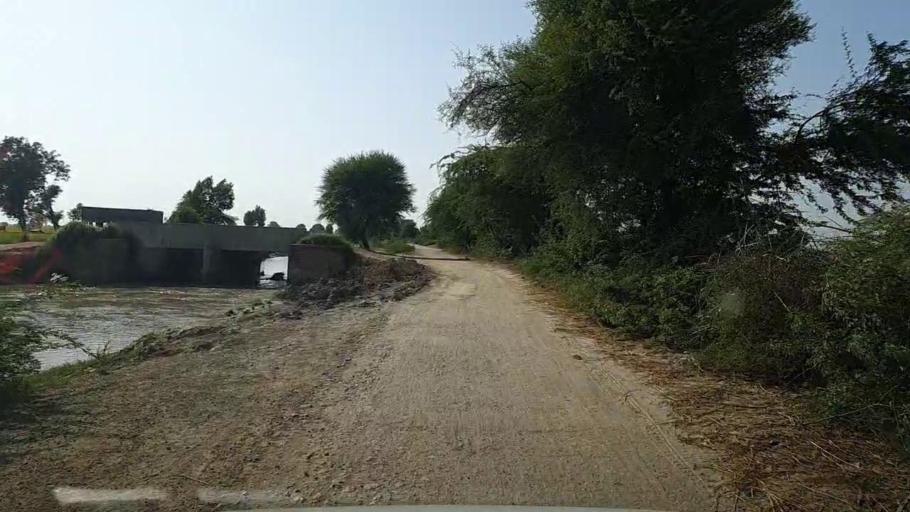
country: PK
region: Sindh
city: Kario
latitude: 24.8057
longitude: 68.5461
